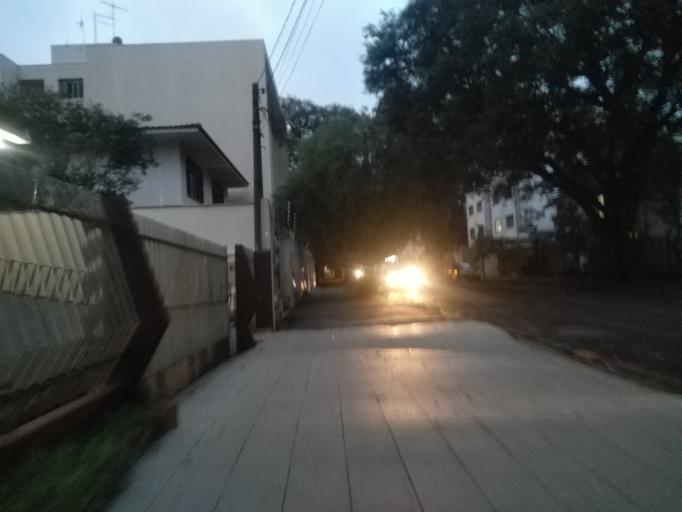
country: BR
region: Parana
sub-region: Maringa
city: Maringa
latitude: -23.4145
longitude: -51.9315
